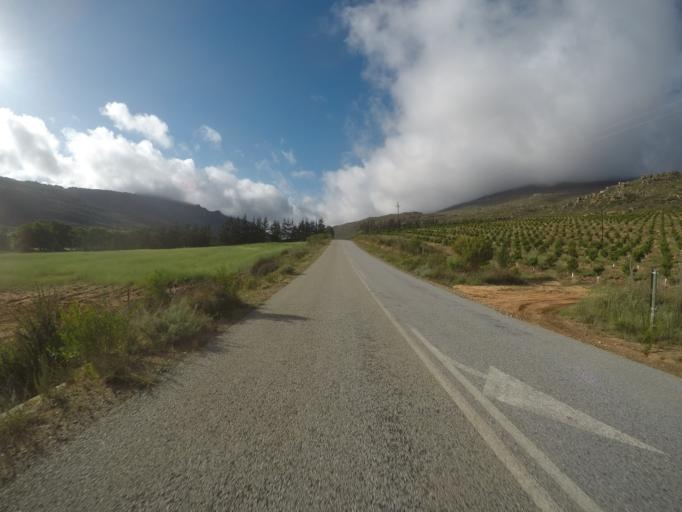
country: ZA
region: Western Cape
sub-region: West Coast District Municipality
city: Clanwilliam
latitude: -32.3573
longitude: 18.8522
